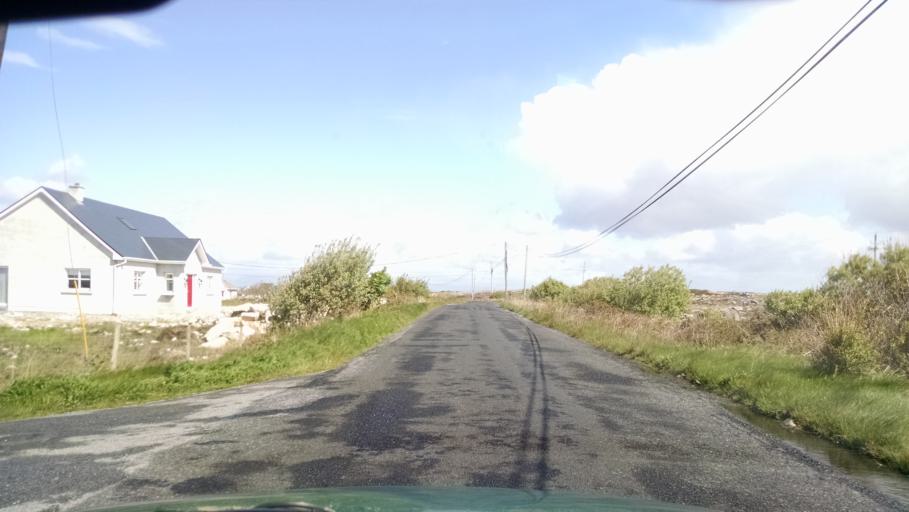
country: IE
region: Connaught
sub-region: County Galway
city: Oughterard
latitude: 53.2544
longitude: -9.5424
